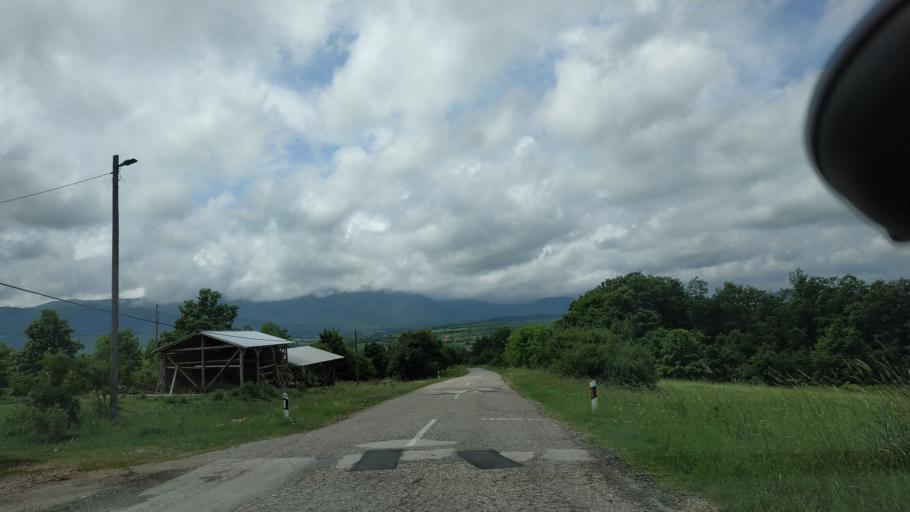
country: RS
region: Central Serbia
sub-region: Zajecarski Okrug
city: Boljevac
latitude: 43.8318
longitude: 21.9726
